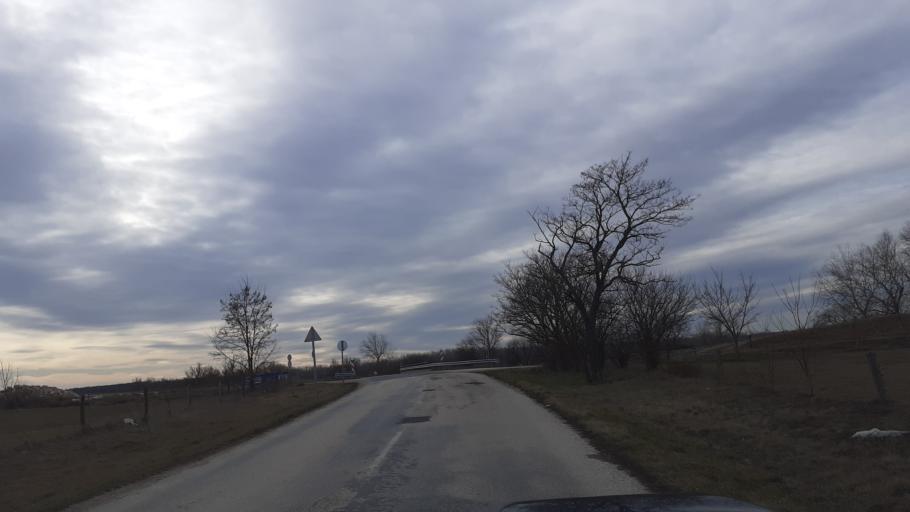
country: HU
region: Fejer
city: Kaloz
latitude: 46.9152
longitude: 18.5406
